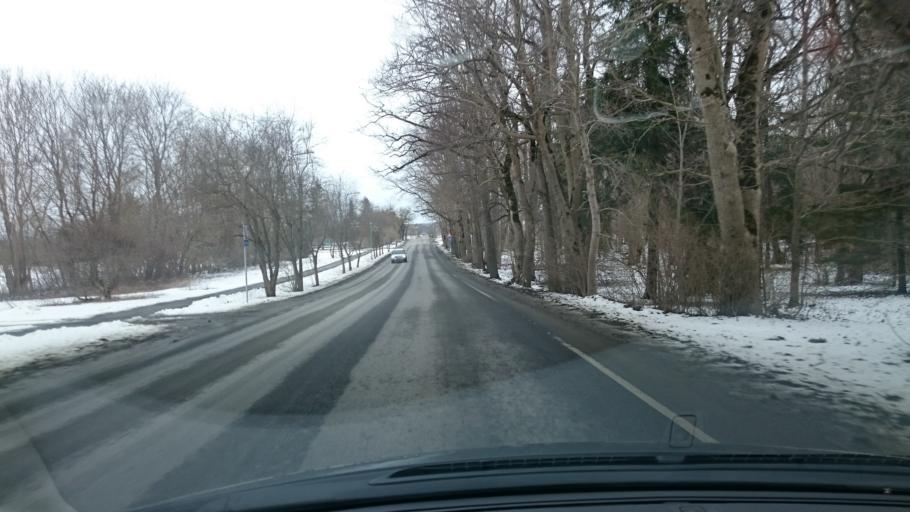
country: EE
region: Harju
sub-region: Saue vald
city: Laagri
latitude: 59.3857
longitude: 24.5765
